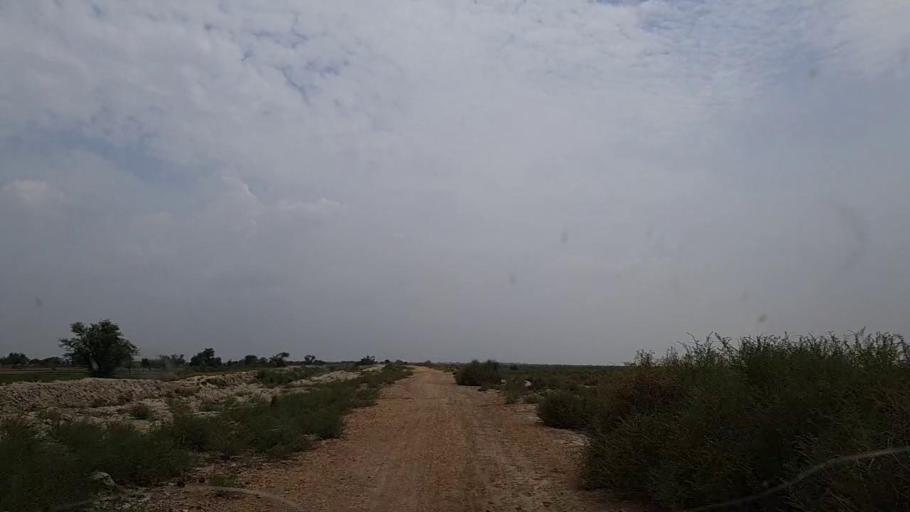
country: PK
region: Sindh
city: Phulji
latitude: 26.8442
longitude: 67.6186
